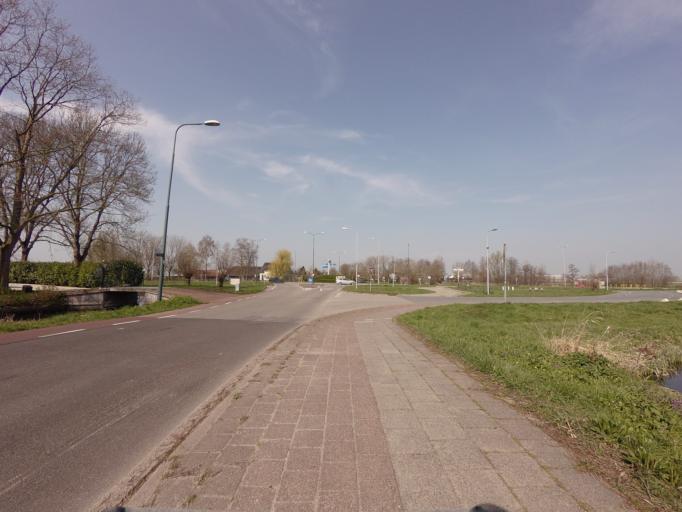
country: NL
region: Utrecht
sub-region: Stichtse Vecht
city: Breukelen
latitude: 52.1577
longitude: 4.9616
